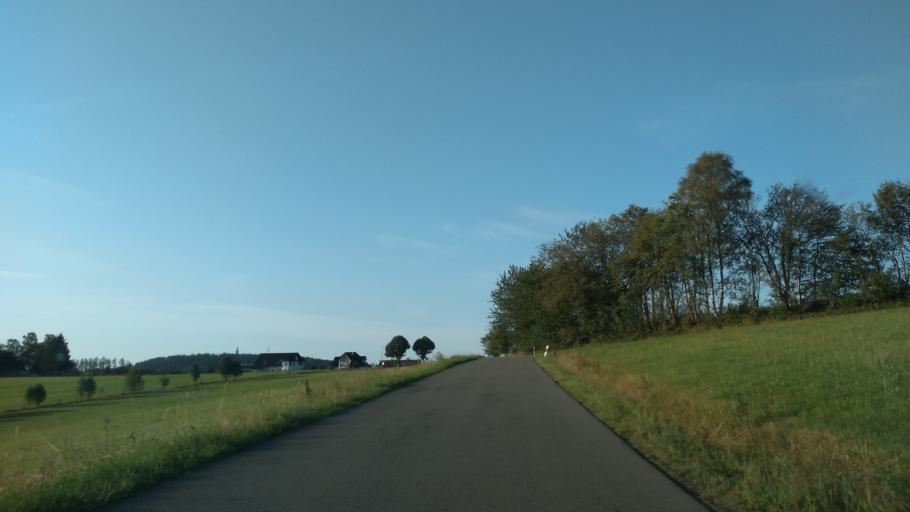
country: DE
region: North Rhine-Westphalia
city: Kierspe
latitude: 51.0792
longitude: 7.5982
